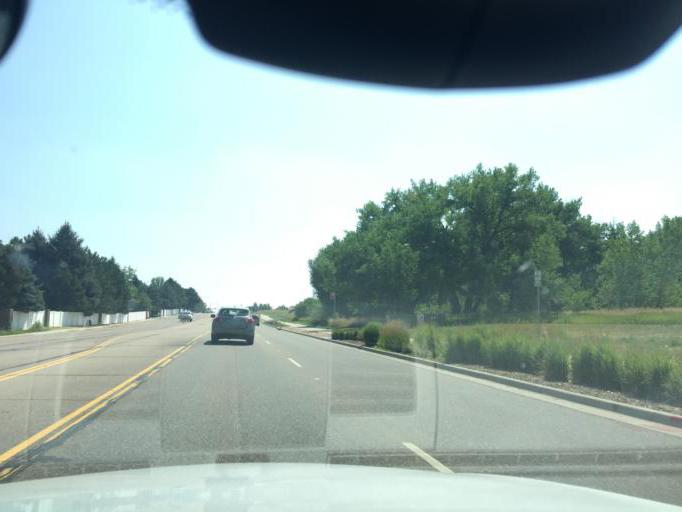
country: US
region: Colorado
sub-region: Adams County
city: Northglenn
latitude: 39.8996
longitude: -105.0113
